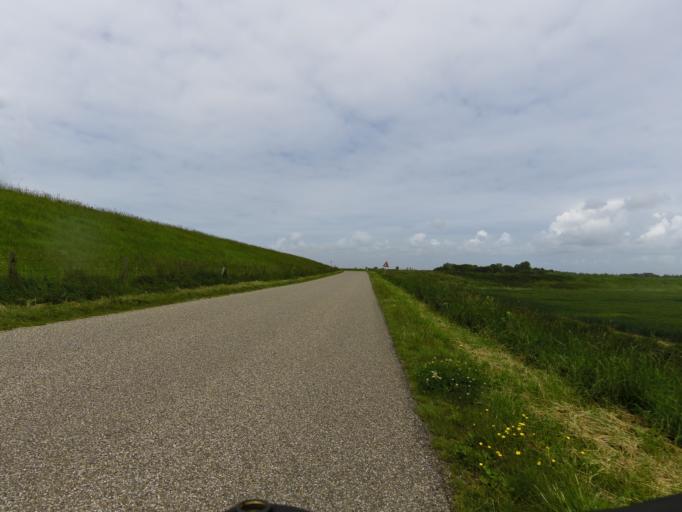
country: NL
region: Zeeland
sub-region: Schouwen-Duiveland
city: Bruinisse
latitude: 51.6311
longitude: 4.0508
